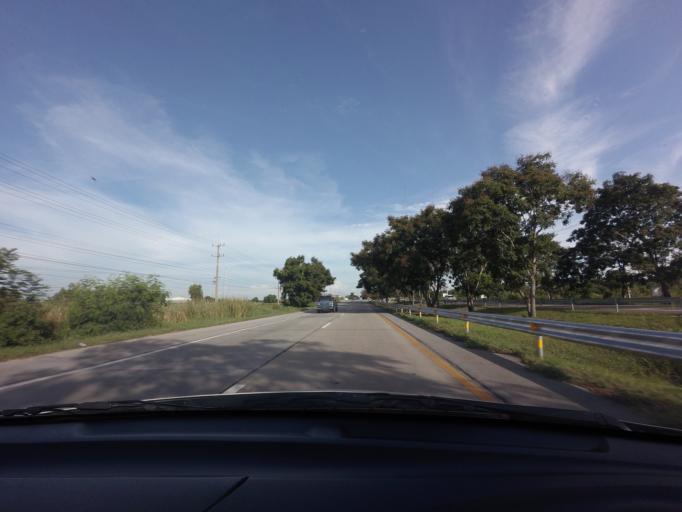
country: TH
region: Phra Nakhon Si Ayutthaya
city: Lat Bua Luang
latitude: 14.2201
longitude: 100.2807
